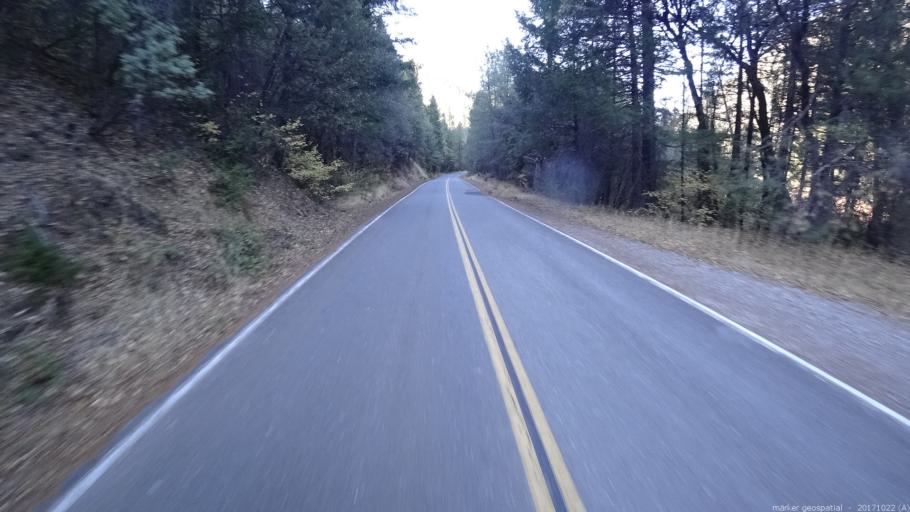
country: US
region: California
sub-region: Siskiyou County
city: Dunsmuir
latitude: 40.9314
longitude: -122.2510
